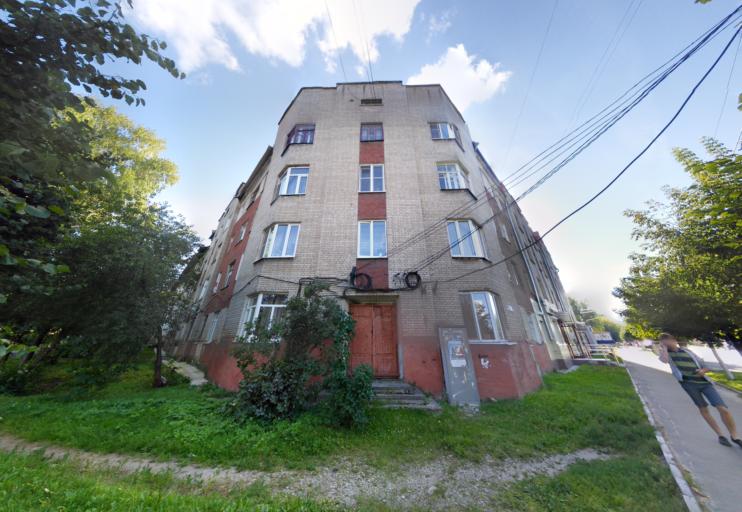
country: RU
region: Moskovskaya
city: Pavlovskiy Posad
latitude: 55.7802
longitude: 38.6634
